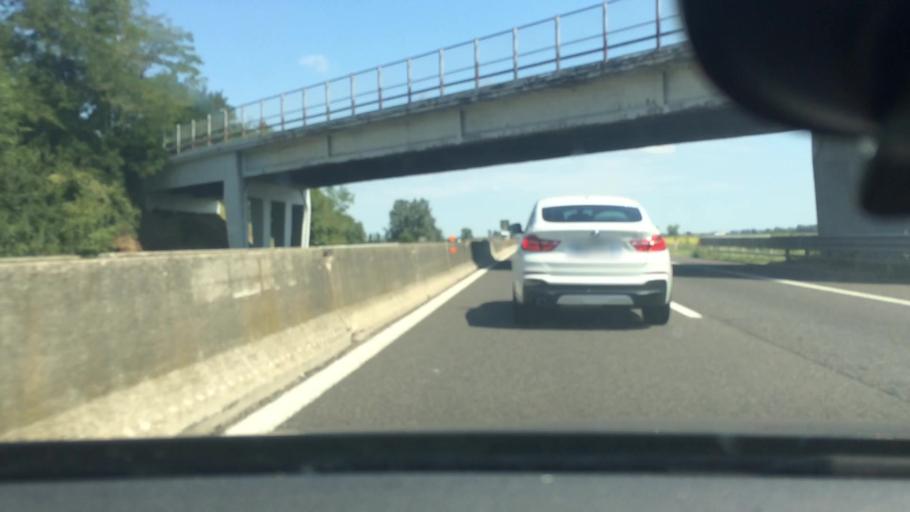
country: IT
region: Emilia-Romagna
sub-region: Provincia di Bologna
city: Altedo
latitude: 44.6607
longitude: 11.4556
